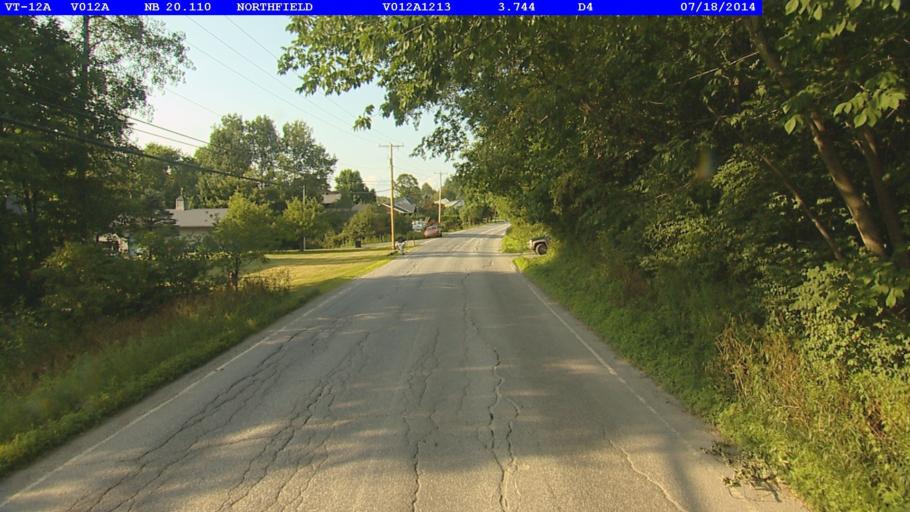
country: US
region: Vermont
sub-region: Washington County
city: Northfield
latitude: 44.1247
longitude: -72.6639
